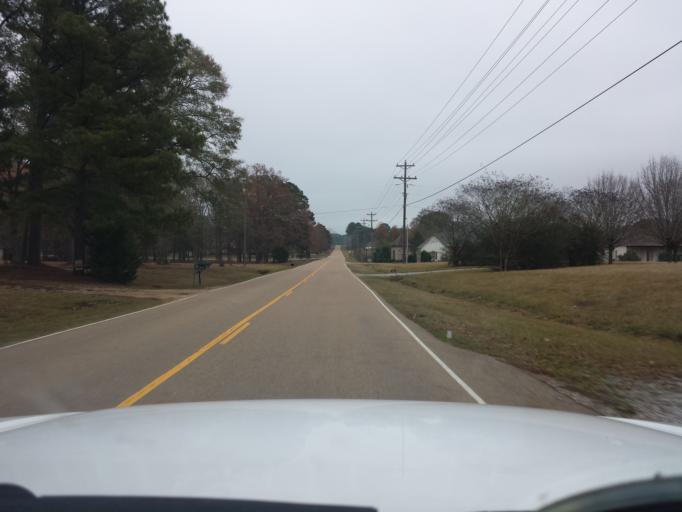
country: US
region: Mississippi
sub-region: Madison County
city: Madison
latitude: 32.4214
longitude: -89.9765
